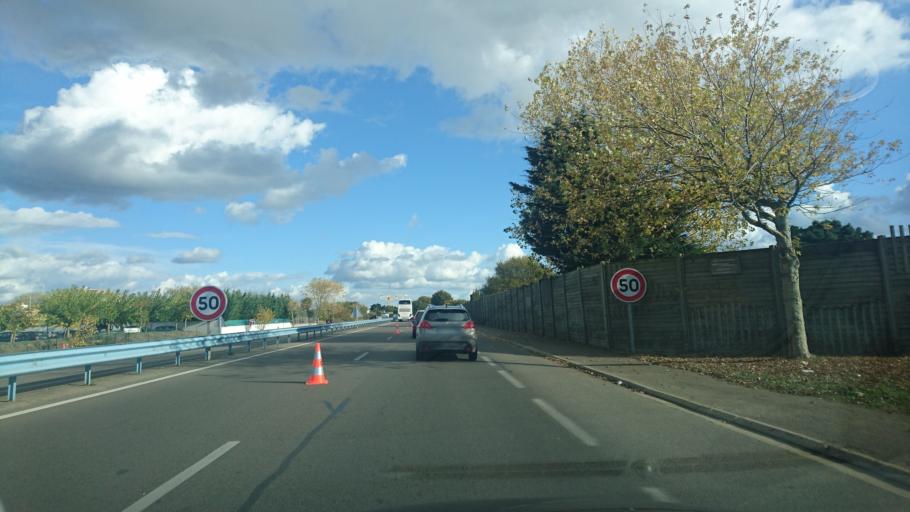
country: FR
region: Pays de la Loire
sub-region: Departement de la Vendee
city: Les Sables-d'Olonne
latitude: 46.5131
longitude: -1.7757
